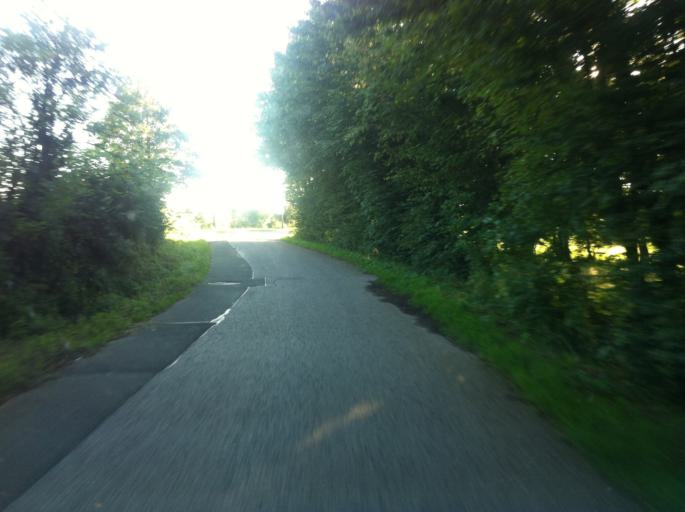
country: DE
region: Rheinland-Pfalz
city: Scheid
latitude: 50.4112
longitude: 6.3754
